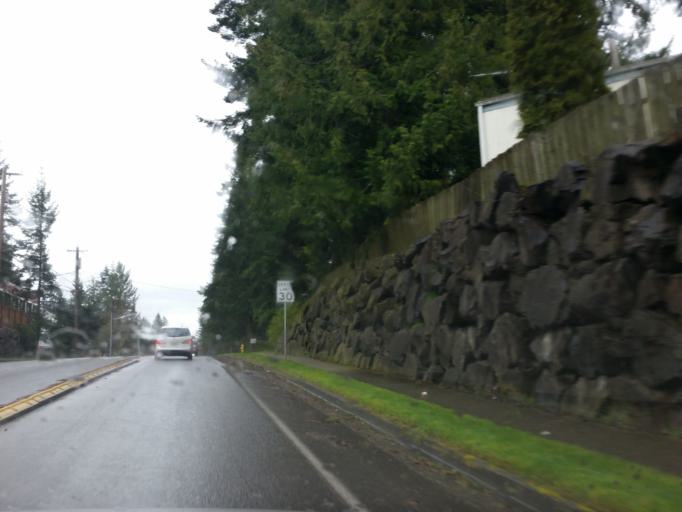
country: US
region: Washington
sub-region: Snohomish County
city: Lynnwood
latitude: 47.8175
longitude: -122.3138
